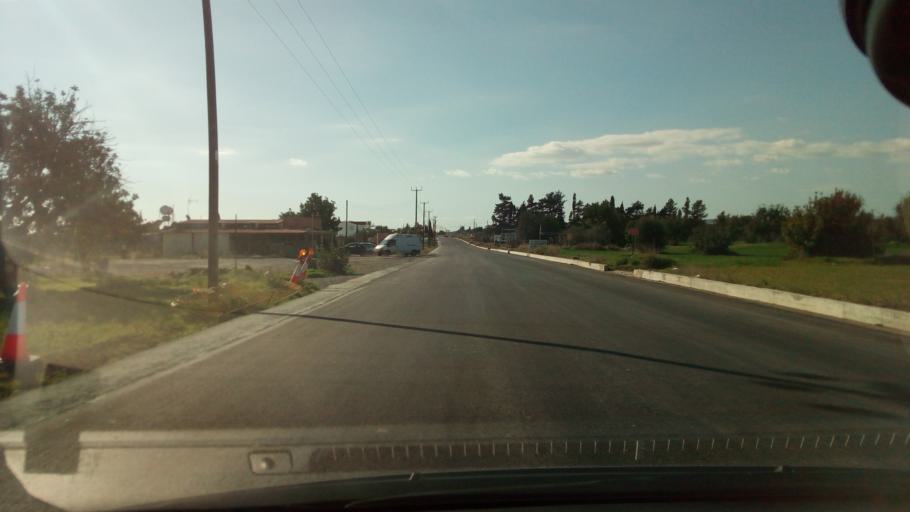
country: CY
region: Larnaka
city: Tersefanou
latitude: 34.8032
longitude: 33.5111
